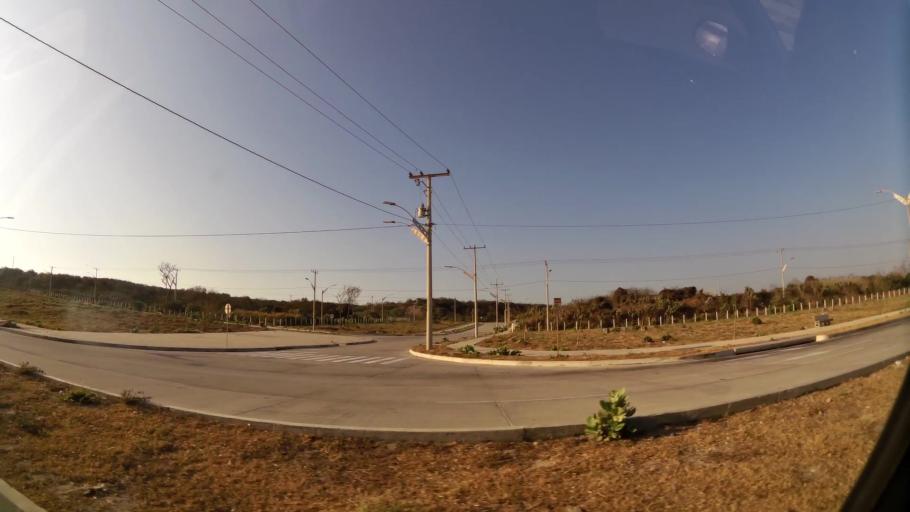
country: CO
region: Atlantico
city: Barranquilla
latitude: 11.0321
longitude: -74.8300
